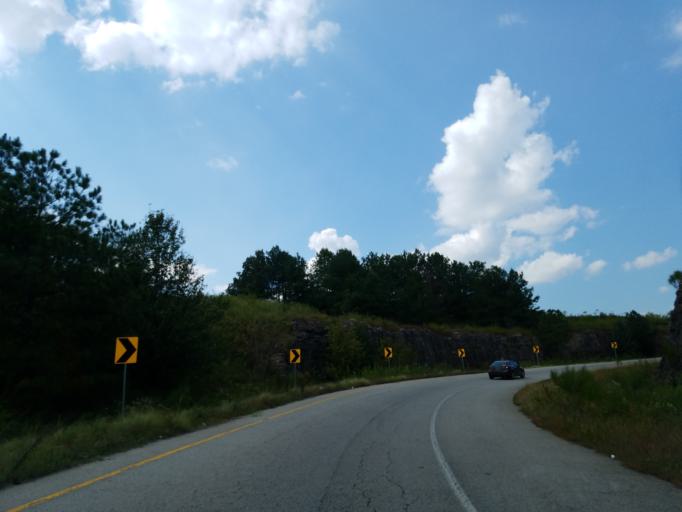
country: US
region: Georgia
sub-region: Gwinnett County
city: Sugar Hill
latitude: 34.0553
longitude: -83.9952
